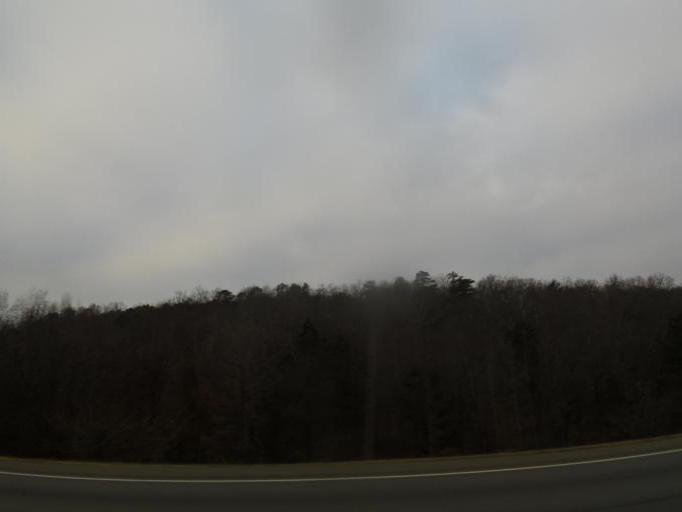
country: US
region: Alabama
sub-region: Jefferson County
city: Gardendale
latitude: 33.6387
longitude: -86.8268
